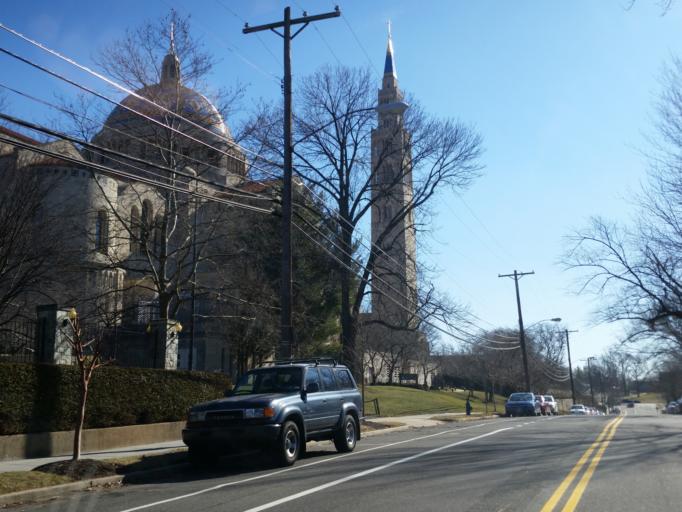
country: US
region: Maryland
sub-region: Prince George's County
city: Chillum
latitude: 38.9343
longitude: -77.0018
